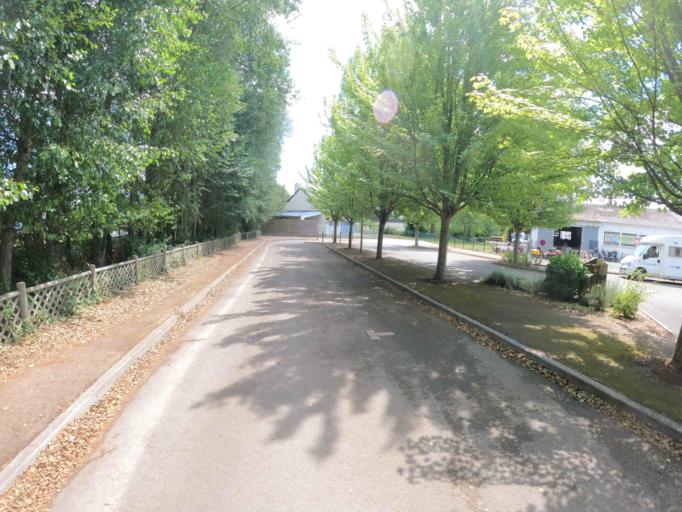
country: FR
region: Pays de la Loire
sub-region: Departement de Maine-et-Loire
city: Champigne
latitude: 47.6617
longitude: -0.5730
